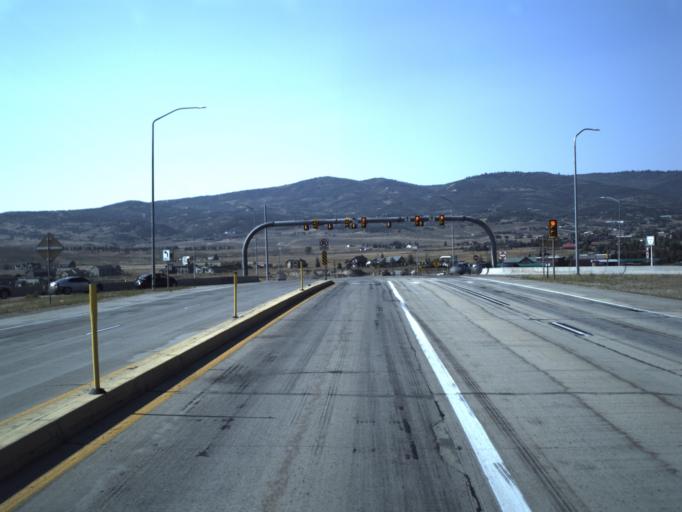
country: US
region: Utah
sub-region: Summit County
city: Snyderville
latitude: 40.7307
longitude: -111.4970
